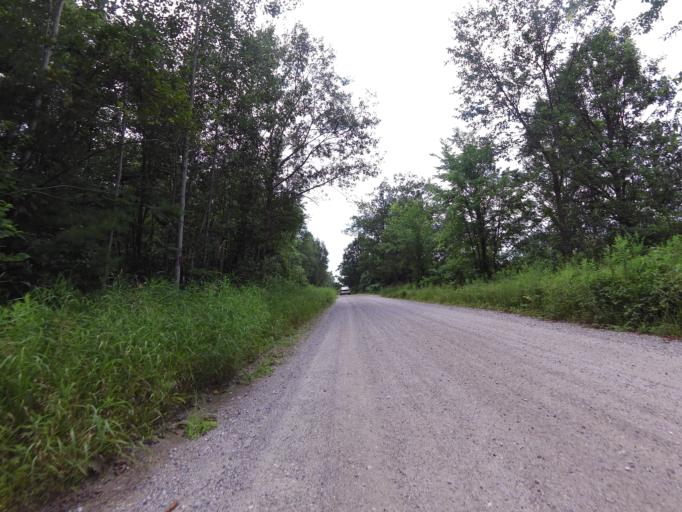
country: CA
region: Ontario
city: Perth
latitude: 44.7387
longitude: -76.6087
